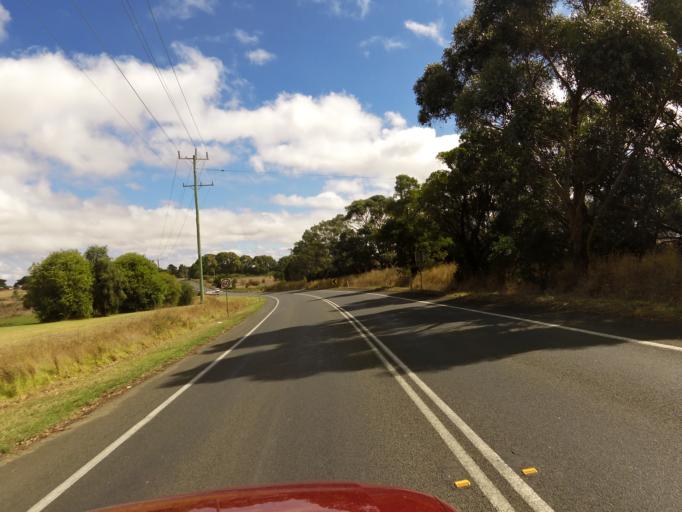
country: AU
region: Victoria
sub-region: Warrnambool
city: Allansford
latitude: -38.2977
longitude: 142.8081
